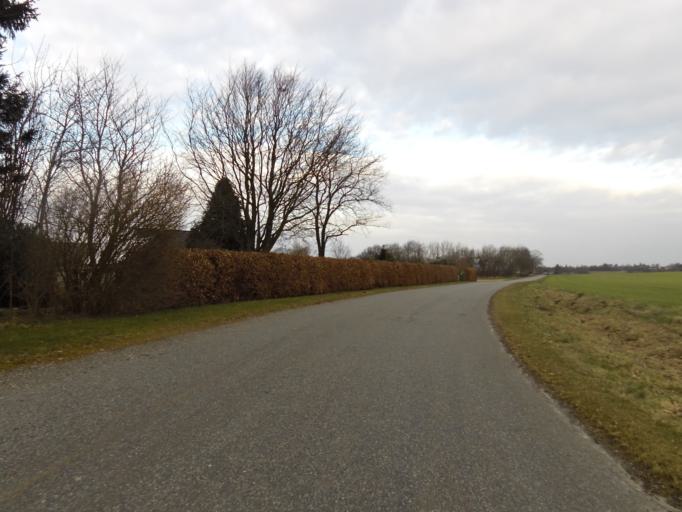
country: DK
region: South Denmark
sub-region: Tonder Kommune
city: Toftlund
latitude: 55.1791
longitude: 9.0451
